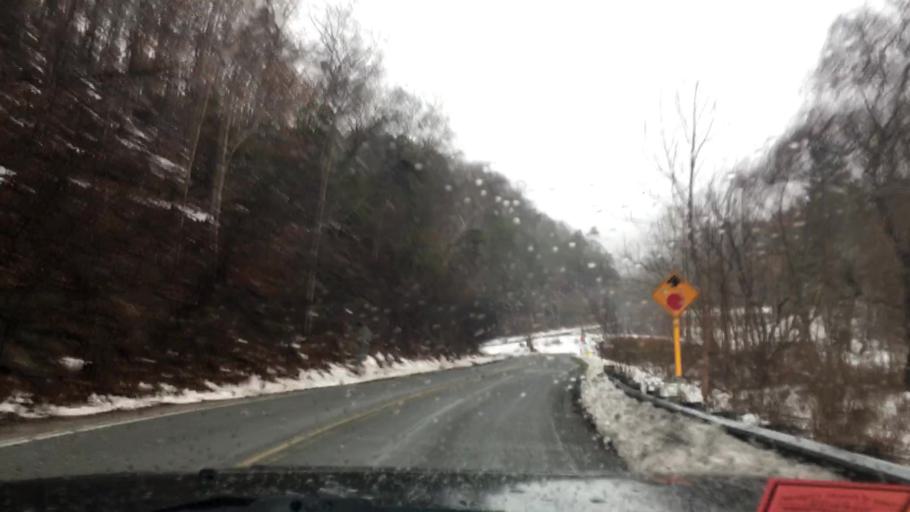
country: US
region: Virginia
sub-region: Pulaski County
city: Dublin
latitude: 37.0013
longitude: -80.6780
